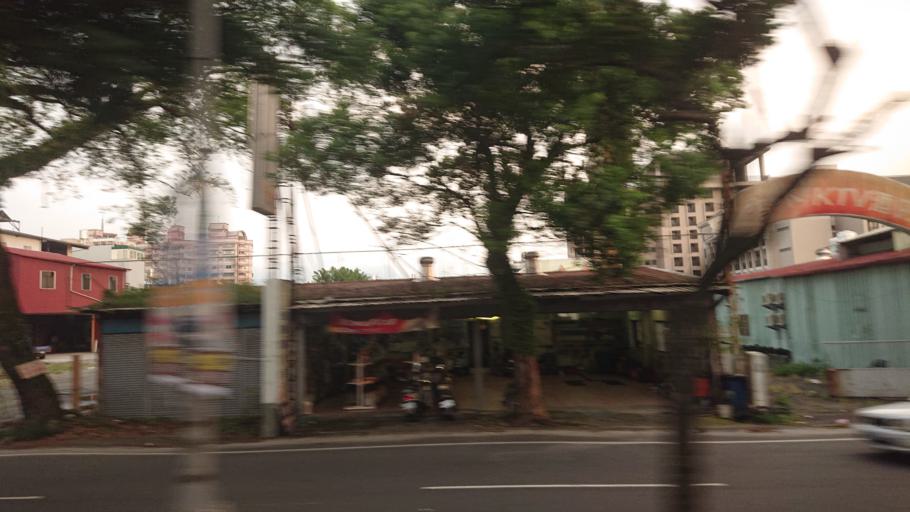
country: TW
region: Taiwan
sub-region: Nantou
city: Puli
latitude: 23.9733
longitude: 120.9665
